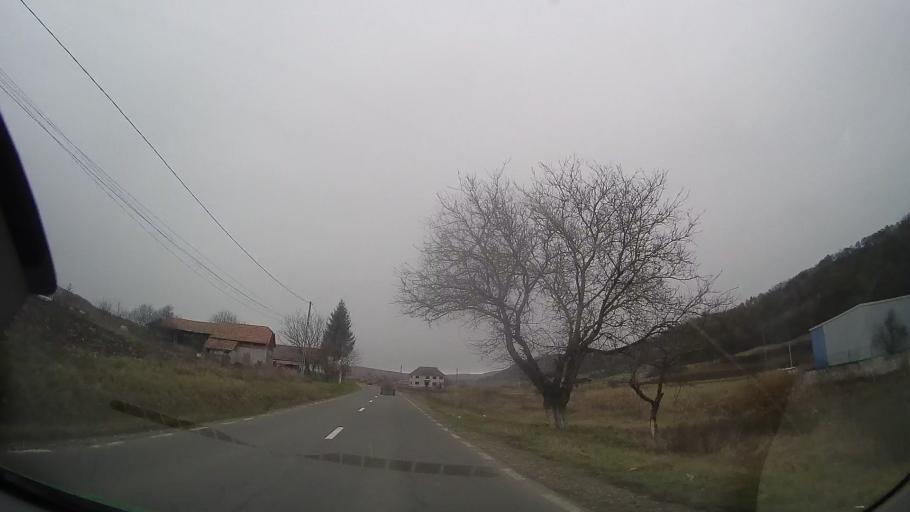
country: RO
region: Mures
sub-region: Comuna Ceausu de Campie
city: Ceausu de Campie
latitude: 46.6197
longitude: 24.5247
